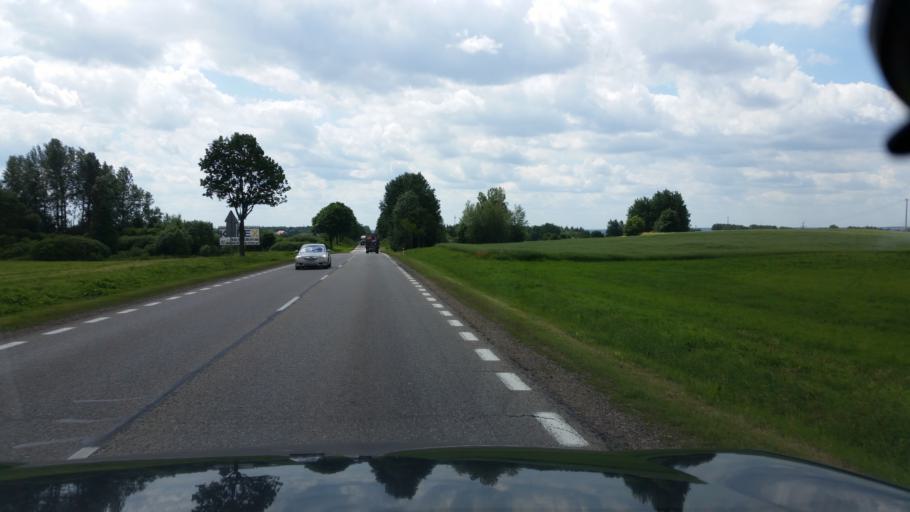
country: PL
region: Podlasie
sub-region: Powiat lomzynski
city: Piatnica
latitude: 53.2250
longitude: 22.1098
